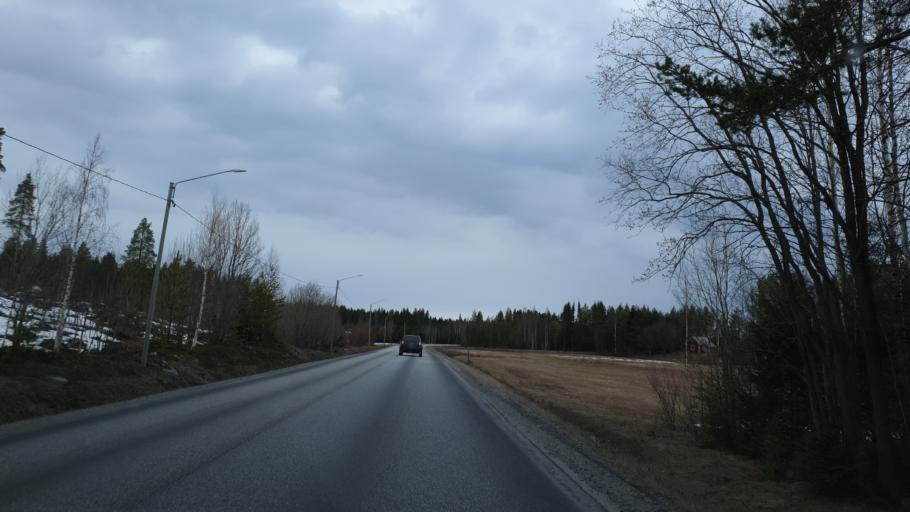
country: SE
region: Vaesterbotten
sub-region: Skelleftea Kommun
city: Viken
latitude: 64.6484
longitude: 20.9575
